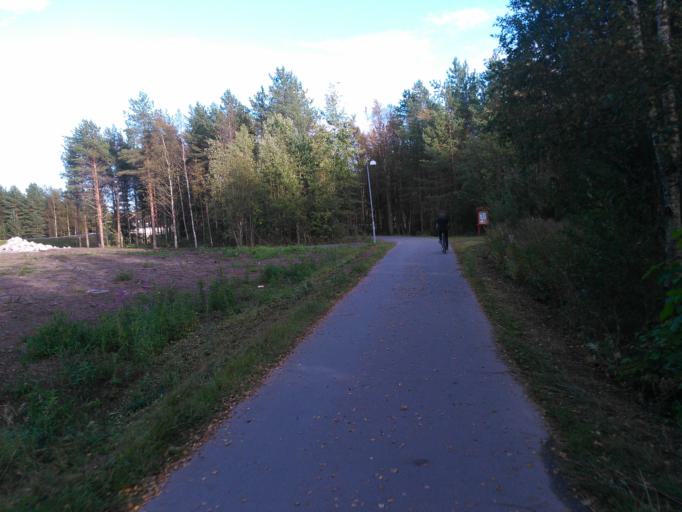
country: SE
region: Vaesterbotten
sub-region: Umea Kommun
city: Umea
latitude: 63.8091
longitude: 20.3318
